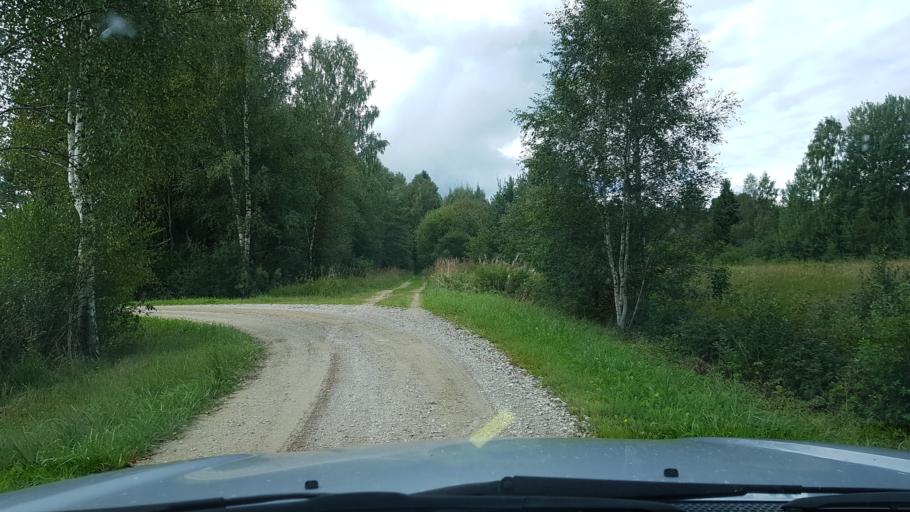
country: EE
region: Harju
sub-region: Raasiku vald
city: Arukula
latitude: 59.2910
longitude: 25.0545
